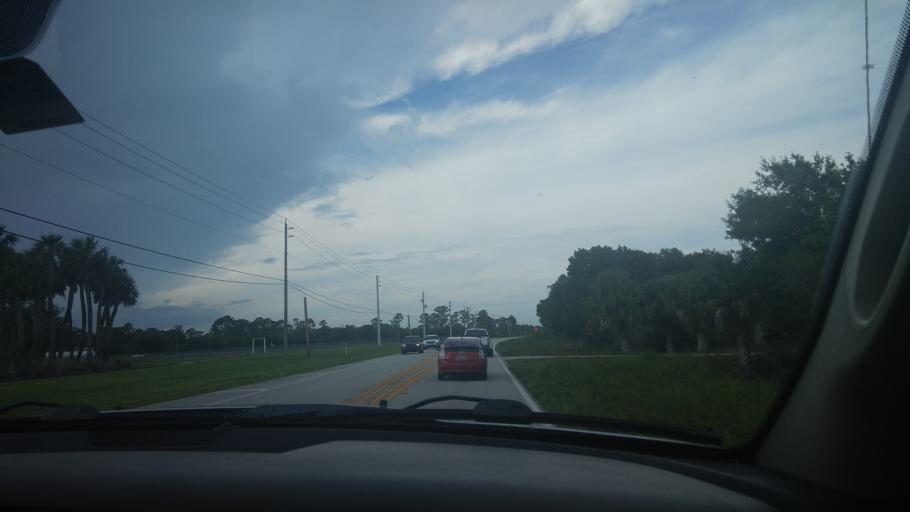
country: US
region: Florida
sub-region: Brevard County
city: Grant-Valkaria
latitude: 27.9076
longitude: -80.6230
